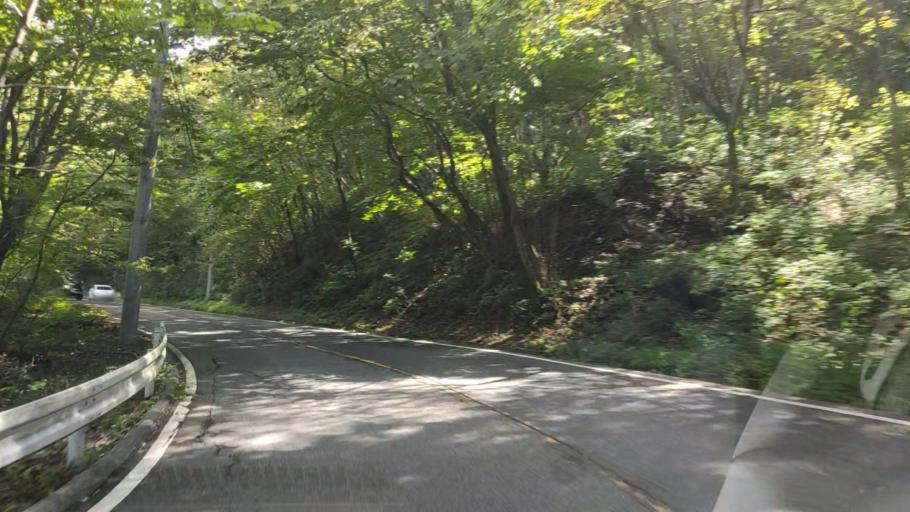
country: JP
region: Gunma
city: Shibukawa
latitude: 36.4930
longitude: 138.9016
